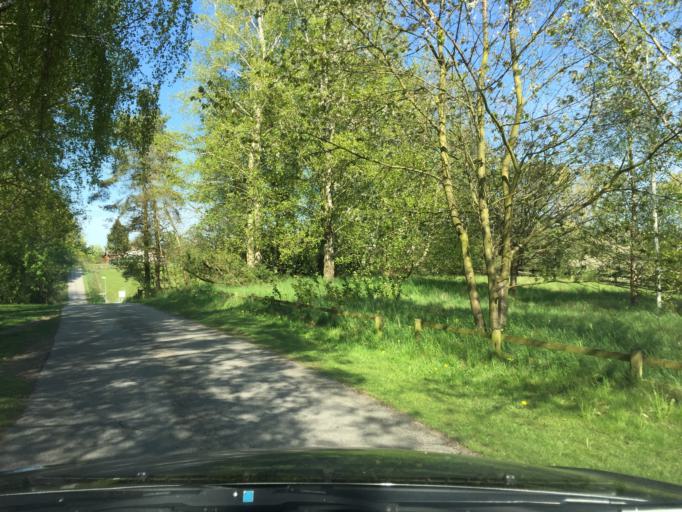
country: SE
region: Skane
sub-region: Sjobo Kommun
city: Blentarp
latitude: 55.5798
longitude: 13.6016
